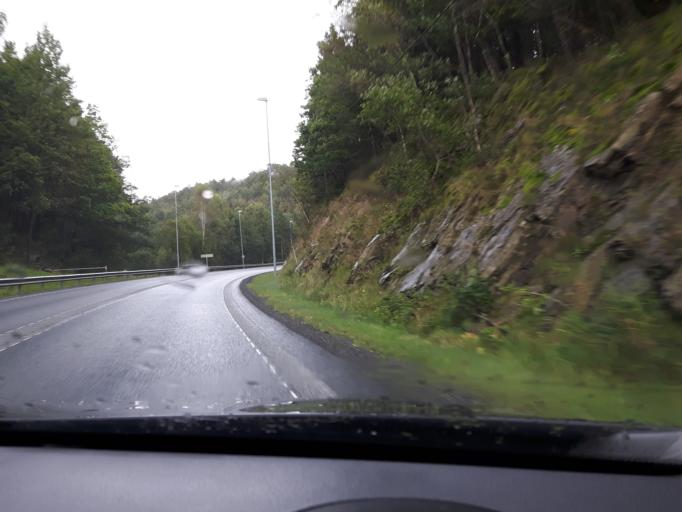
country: NO
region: Vest-Agder
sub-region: Marnardal
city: Helland
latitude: 58.0941
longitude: 7.6300
